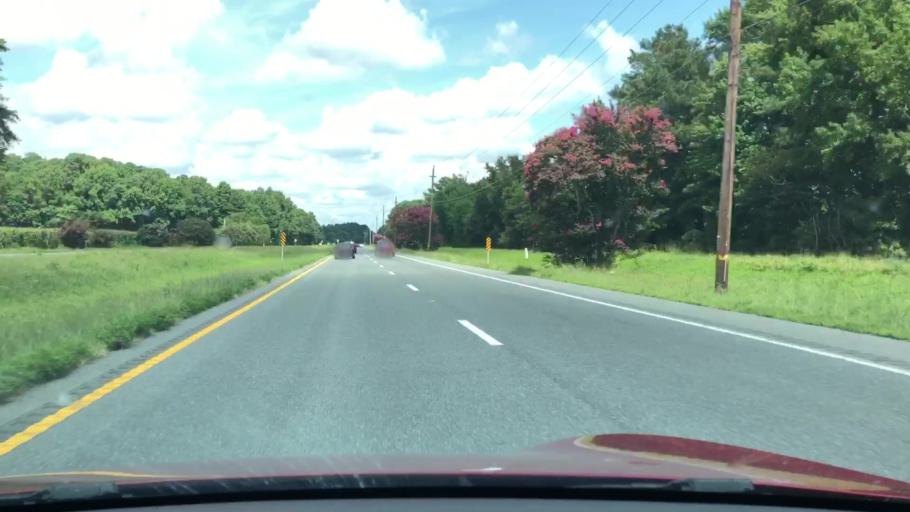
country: US
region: Virginia
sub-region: Northampton County
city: Eastville
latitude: 37.4140
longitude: -75.8978
